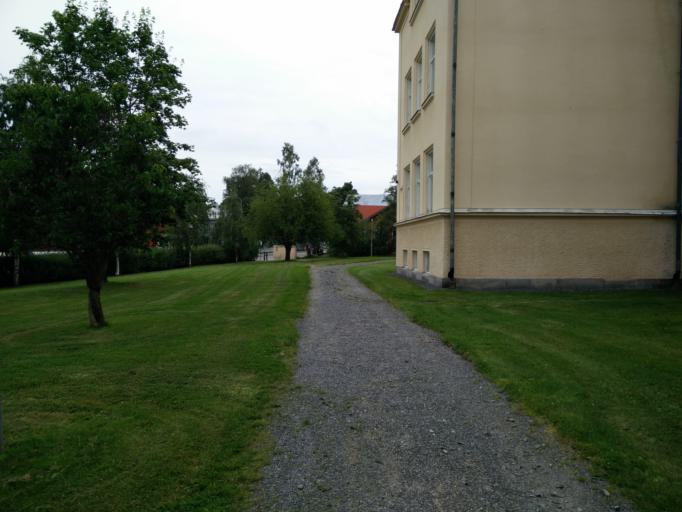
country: SE
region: Vaesternorrland
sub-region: Haernoesands Kommun
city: Haernoesand
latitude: 62.6321
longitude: 17.9498
